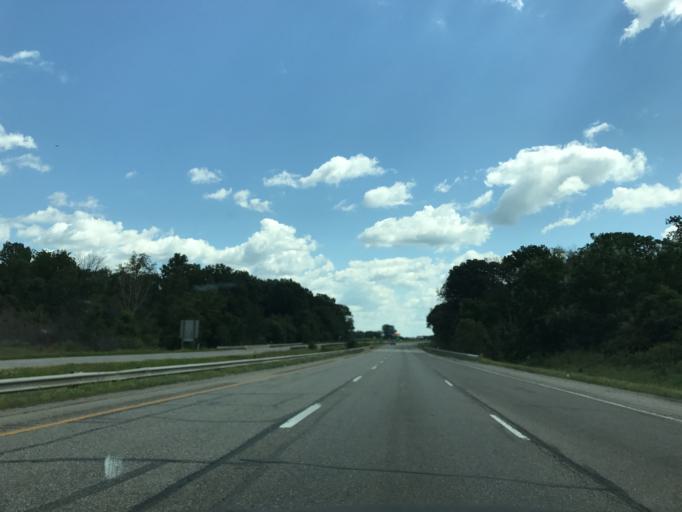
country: US
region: Indiana
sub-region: Marshall County
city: Plymouth
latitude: 41.3621
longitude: -86.3084
